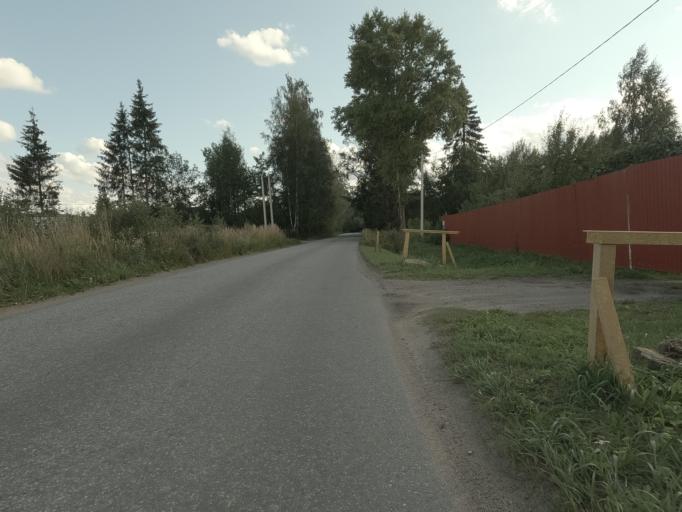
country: RU
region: Leningrad
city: Ul'yanovka
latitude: 59.6298
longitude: 30.7938
